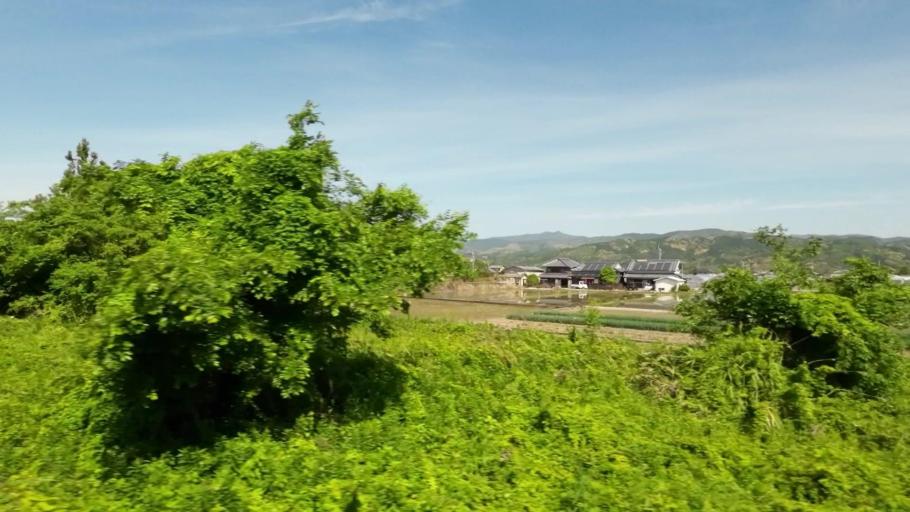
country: JP
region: Kochi
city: Kochi-shi
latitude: 33.6023
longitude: 133.6746
